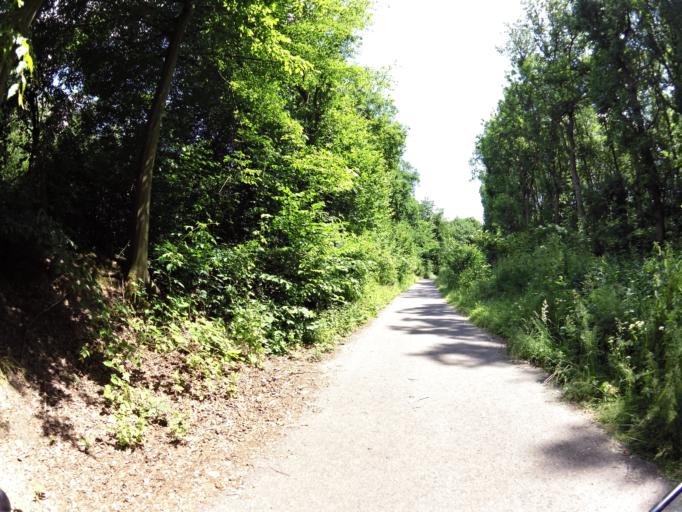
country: NL
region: Limburg
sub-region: Gemeente Echt-Susteren
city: Koningsbosch
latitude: 51.0279
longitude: 5.9738
